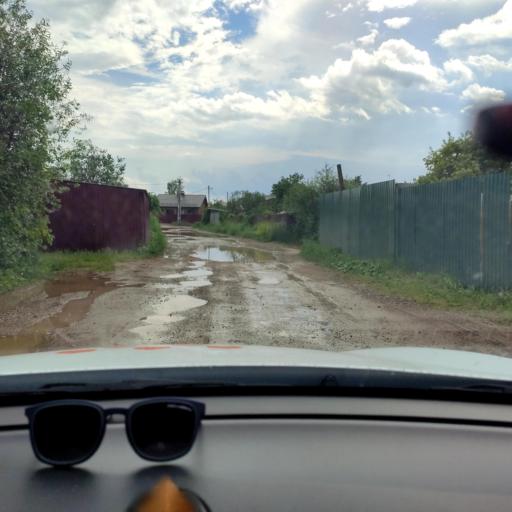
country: RU
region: Tatarstan
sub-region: Zelenodol'skiy Rayon
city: Vasil'yevo
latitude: 55.8244
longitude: 48.7246
